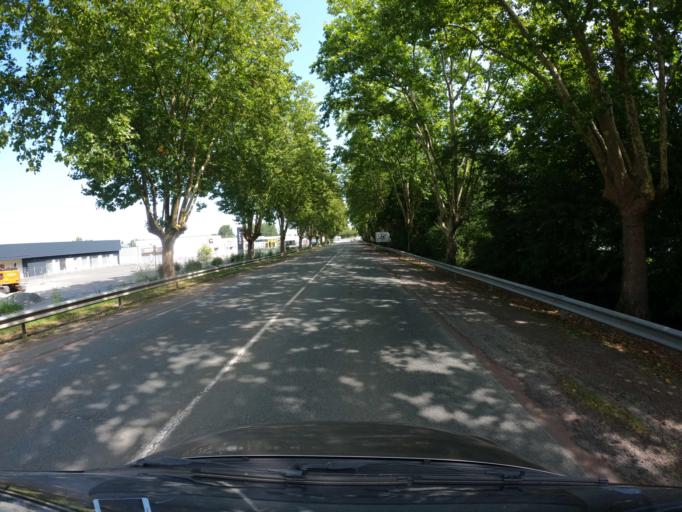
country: FR
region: Poitou-Charentes
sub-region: Departement des Deux-Sevres
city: Bessines
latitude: 46.3007
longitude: -0.4945
